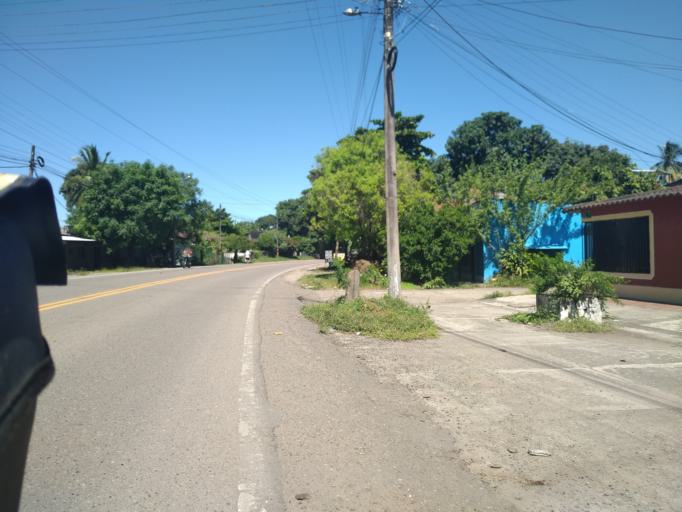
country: CO
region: Cundinamarca
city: Puerto Salgar
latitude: 5.4675
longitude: -74.6522
